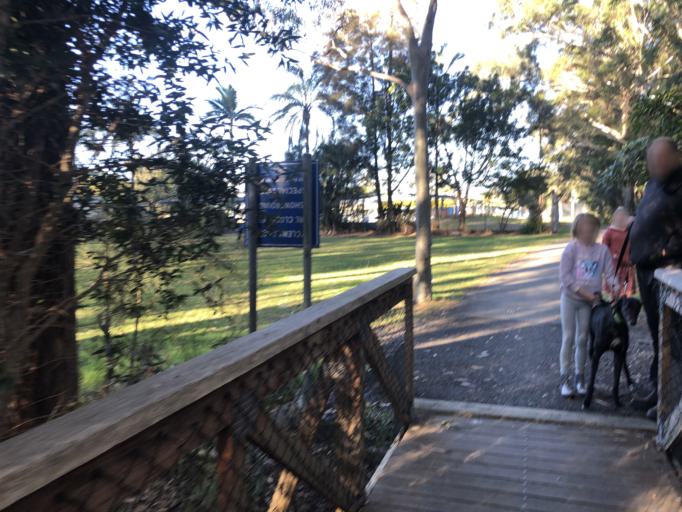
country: AU
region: New South Wales
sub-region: Coffs Harbour
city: Coffs Harbour
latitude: -30.2943
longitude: 153.1193
